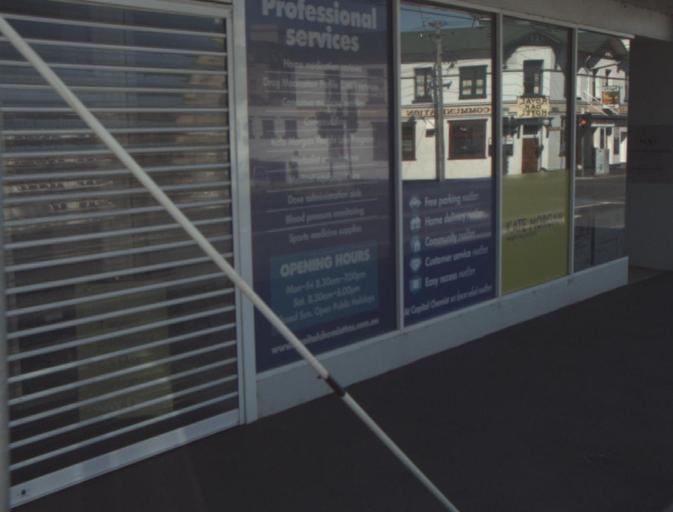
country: AU
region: Tasmania
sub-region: Launceston
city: East Launceston
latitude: -41.4342
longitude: 147.1428
